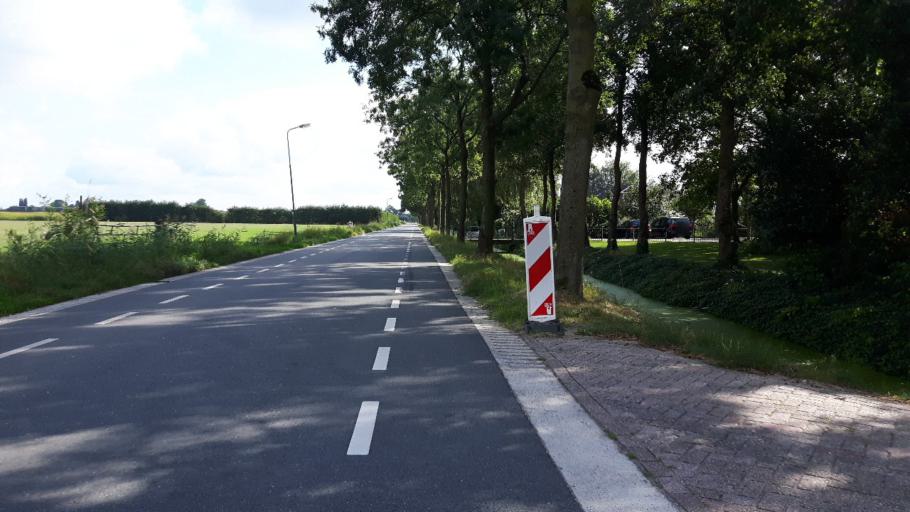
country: NL
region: Utrecht
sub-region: Stichtse Vecht
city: Spechtenkamp
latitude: 52.1001
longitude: 4.9788
